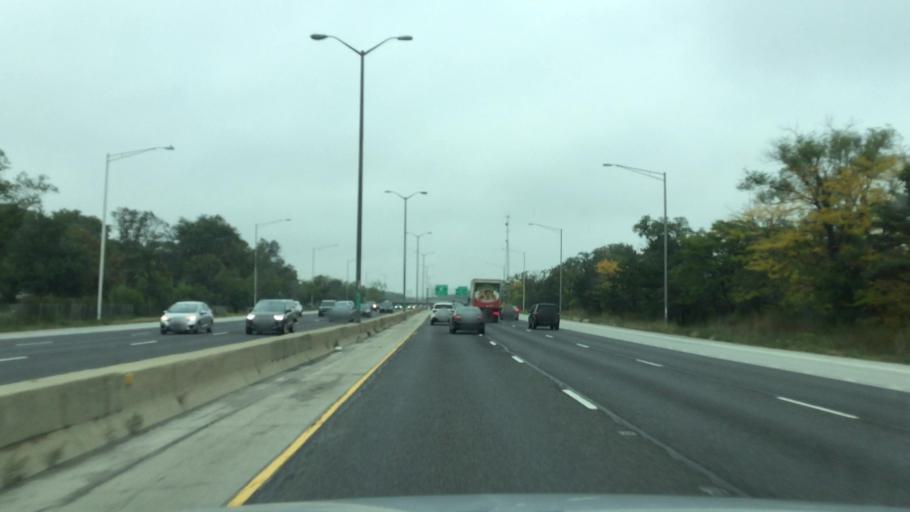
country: US
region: Illinois
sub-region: Cook County
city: Northfield
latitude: 42.0975
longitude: -87.7651
